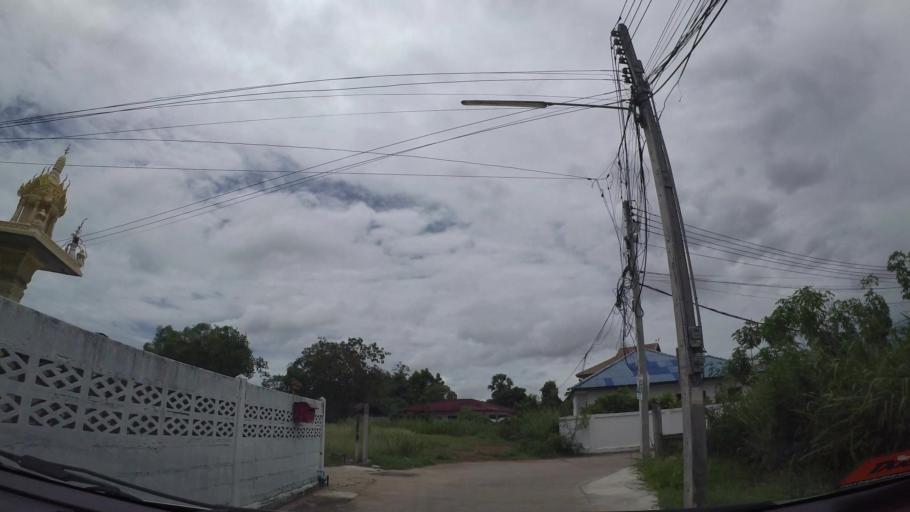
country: TH
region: Chon Buri
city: Sattahip
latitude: 12.7579
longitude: 100.8922
